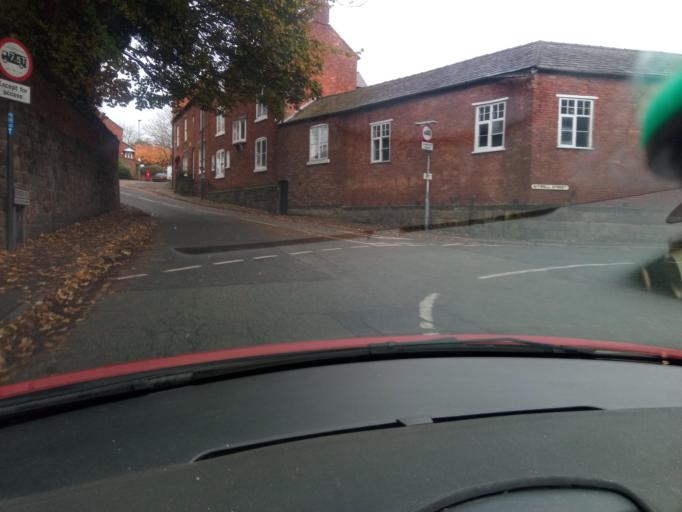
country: GB
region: England
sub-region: Derbyshire
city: Borrowash
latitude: 52.9190
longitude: -1.4090
